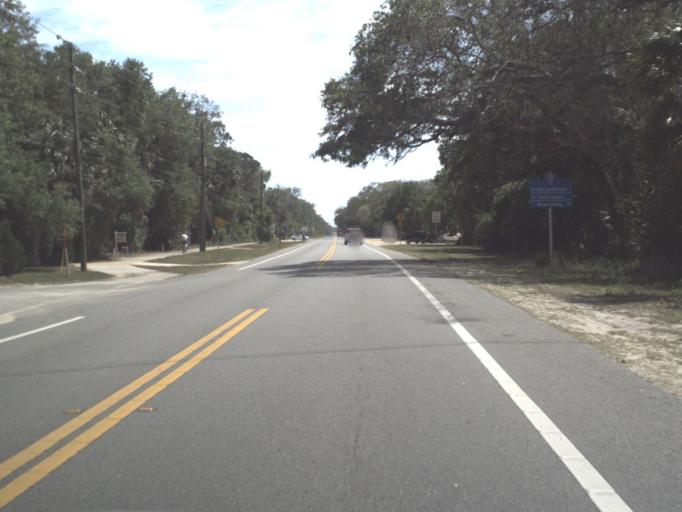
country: US
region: Florida
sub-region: Flagler County
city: Palm Coast
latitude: 29.6174
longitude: -81.2036
